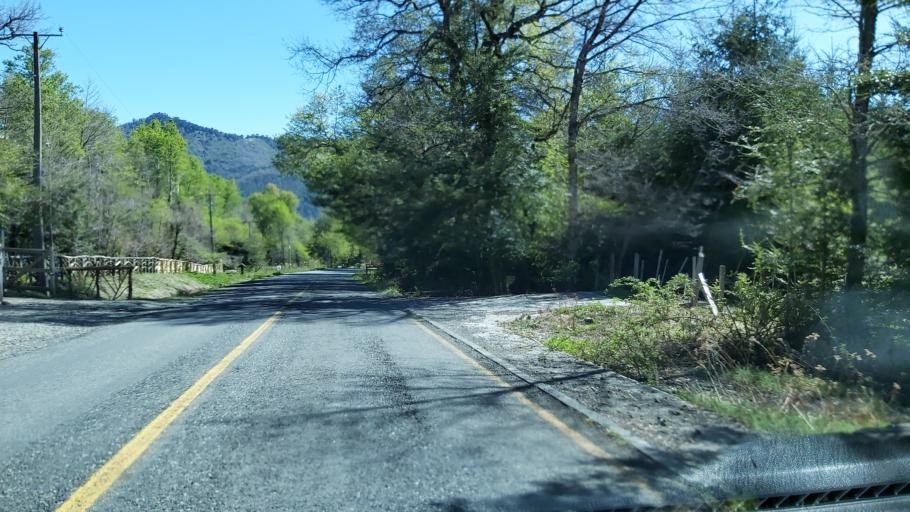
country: CL
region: Araucania
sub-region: Provincia de Cautin
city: Vilcun
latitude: -38.4776
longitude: -71.5337
